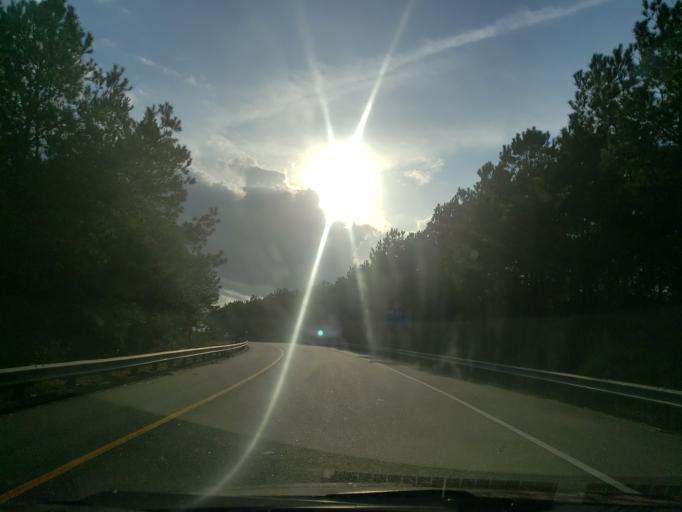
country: US
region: Georgia
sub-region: Chatham County
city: Port Wentworth
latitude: 32.1692
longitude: -81.2161
